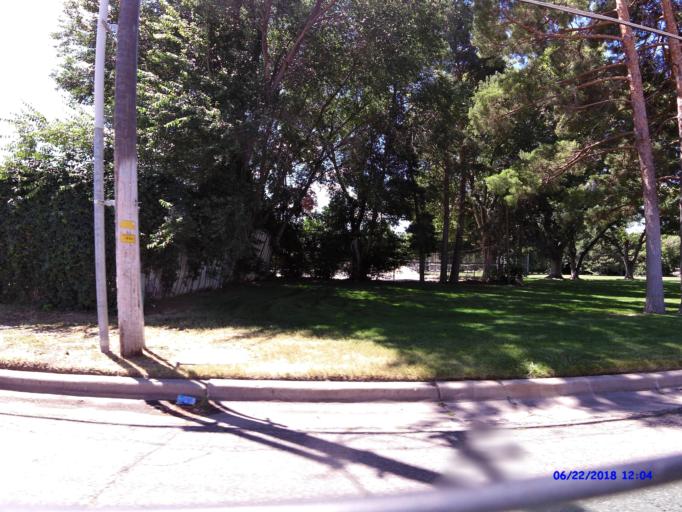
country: US
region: Utah
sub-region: Weber County
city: Ogden
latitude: 41.2376
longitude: -111.9632
